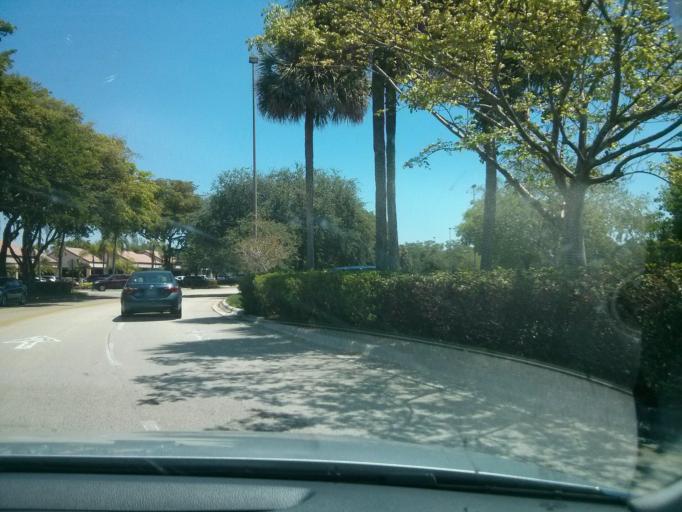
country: US
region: Florida
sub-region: Broward County
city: Tamarac
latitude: 26.2424
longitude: -80.2527
